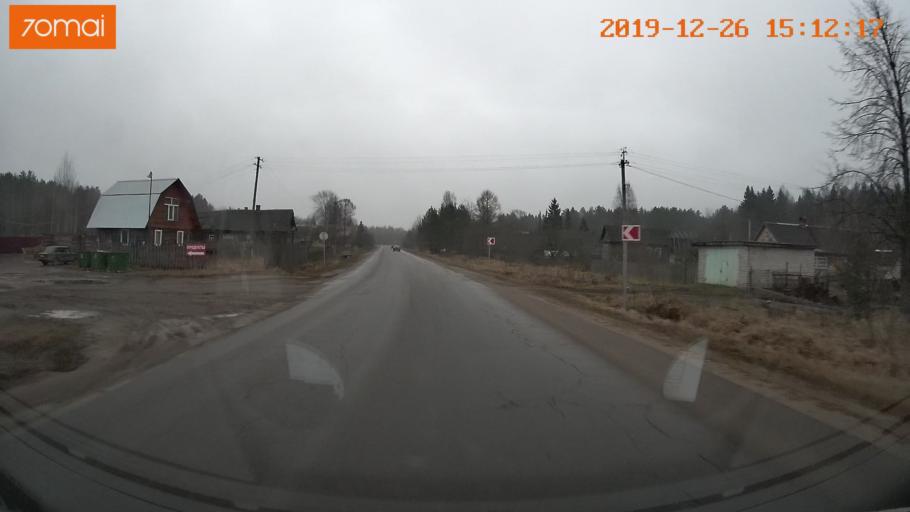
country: RU
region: Jaroslavl
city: Rybinsk
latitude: 58.1284
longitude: 38.8732
